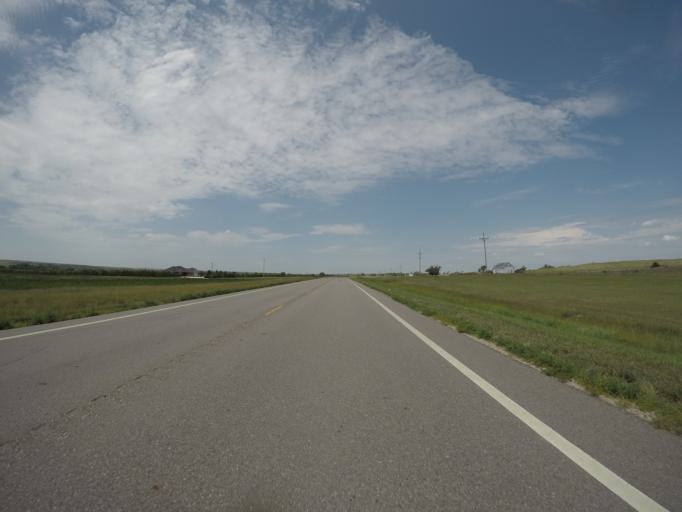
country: US
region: Kansas
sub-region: Rooks County
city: Stockton
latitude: 39.4441
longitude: -99.2107
